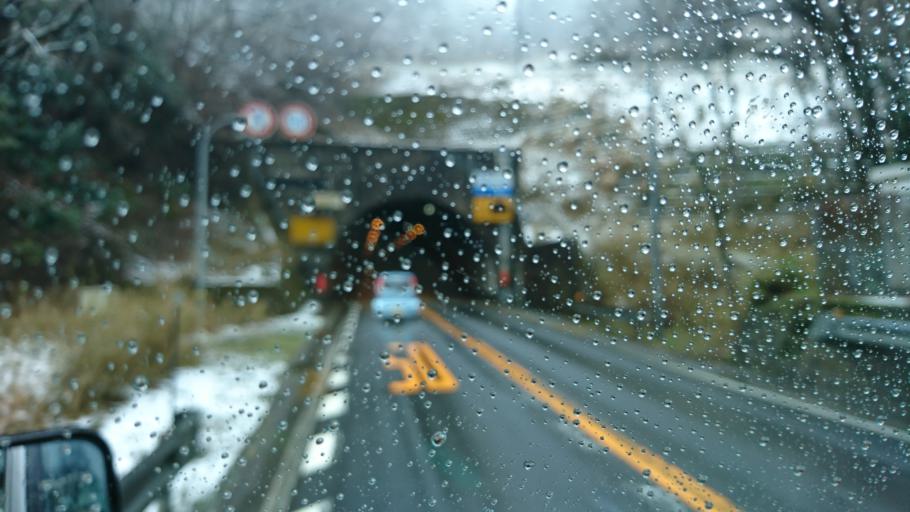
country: JP
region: Hyogo
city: Toyooka
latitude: 35.4816
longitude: 134.5843
